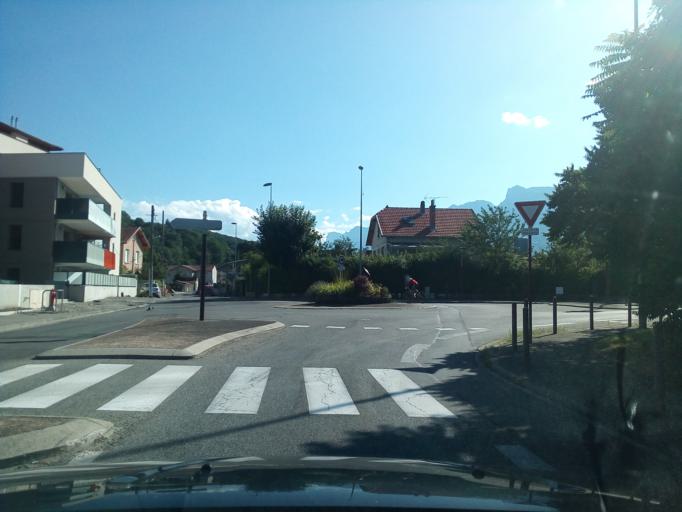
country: FR
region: Rhone-Alpes
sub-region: Departement de l'Isere
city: Echirolles
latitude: 45.1407
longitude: 5.7198
